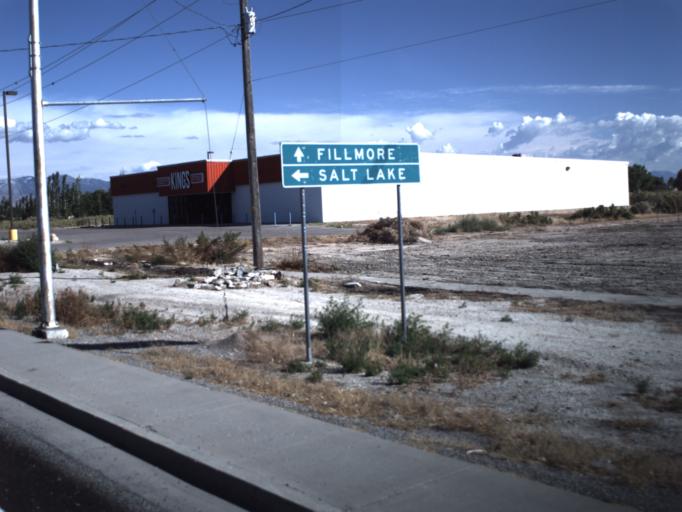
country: US
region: Utah
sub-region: Millard County
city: Delta
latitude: 39.3523
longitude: -112.5652
